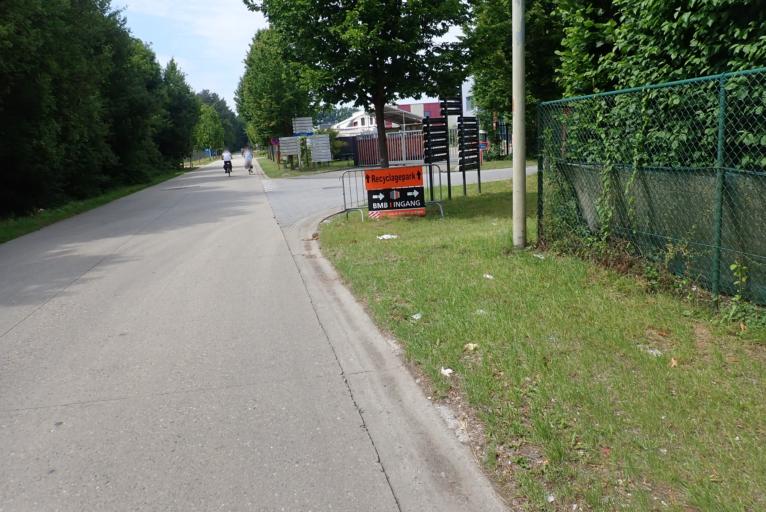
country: BE
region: Flanders
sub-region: Provincie Antwerpen
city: Kalmthout
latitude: 51.3644
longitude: 4.5021
